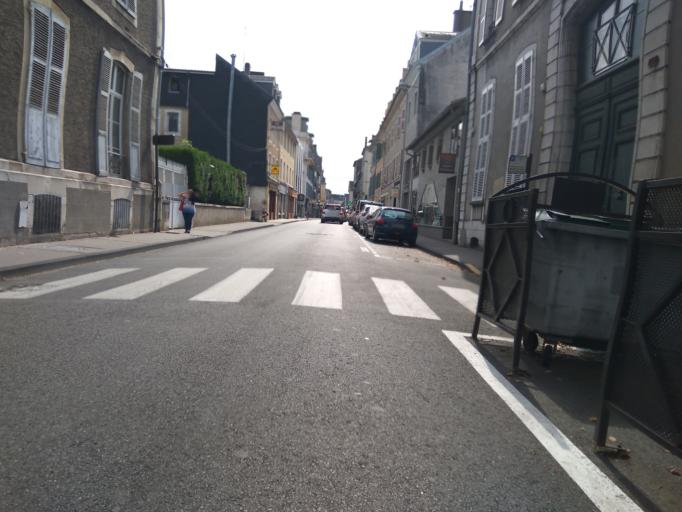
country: FR
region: Aquitaine
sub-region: Departement des Pyrenees-Atlantiques
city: Pau
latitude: 43.3000
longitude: -0.3720
